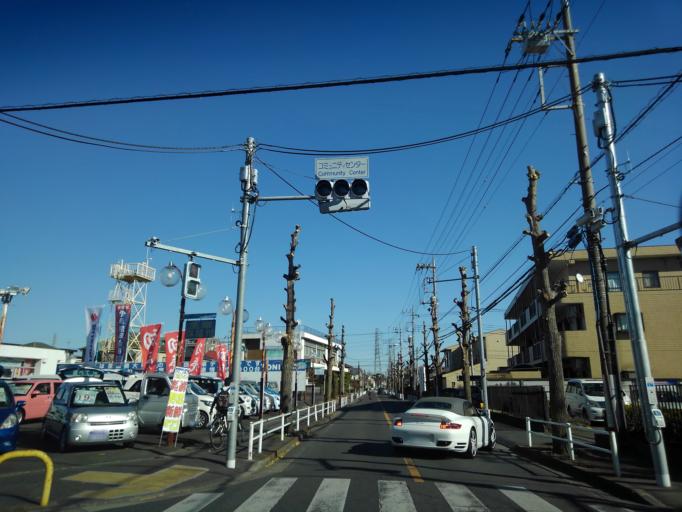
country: JP
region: Tokyo
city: Fussa
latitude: 35.7685
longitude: 139.3109
